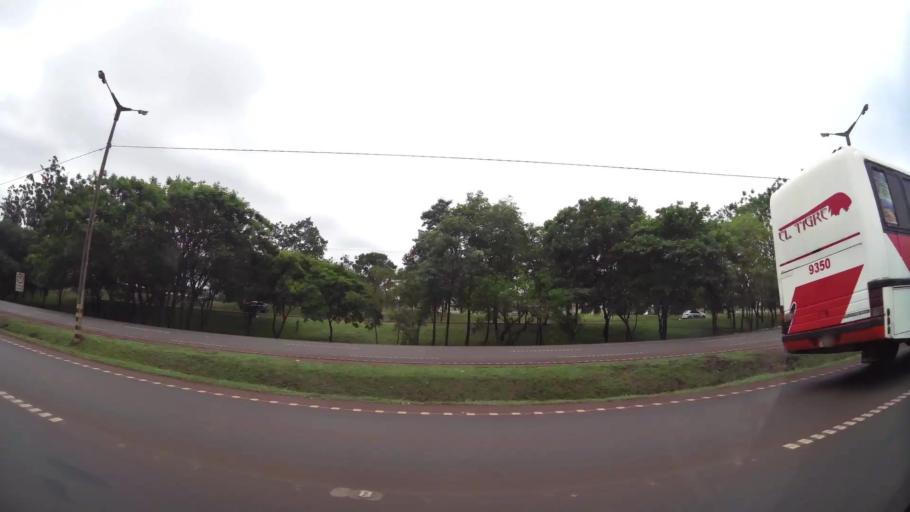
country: PY
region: Alto Parana
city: Ciudad del Este
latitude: -25.4974
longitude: -54.6684
